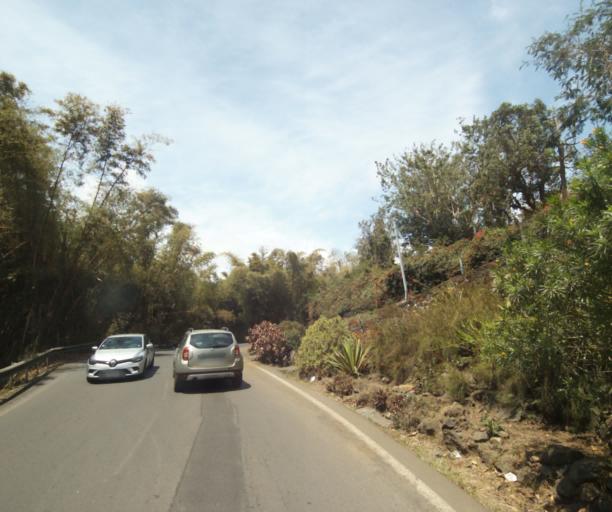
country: RE
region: Reunion
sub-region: Reunion
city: Trois-Bassins
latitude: -21.0832
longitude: 55.2721
